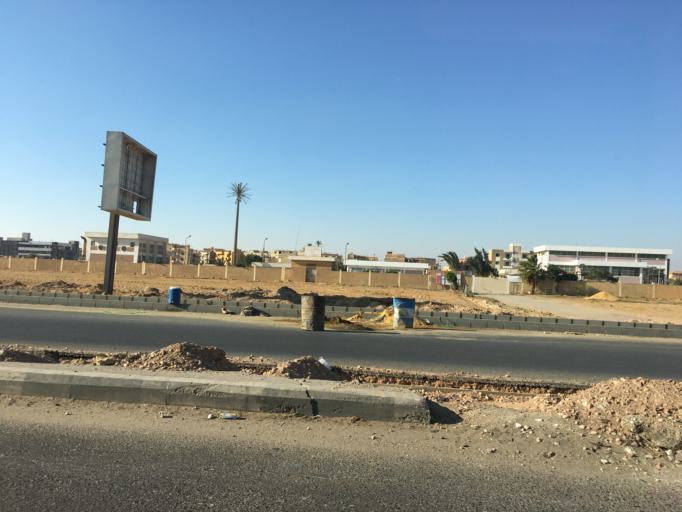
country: EG
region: Al Jizah
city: Madinat Sittah Uktubar
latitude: 29.9927
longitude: 30.9479
